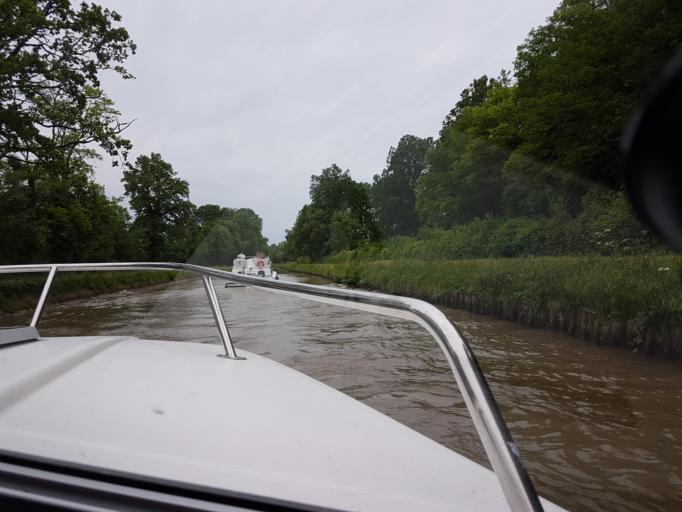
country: FR
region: Bourgogne
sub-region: Departement de la Nievre
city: Clamecy
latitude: 47.4020
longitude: 3.6059
